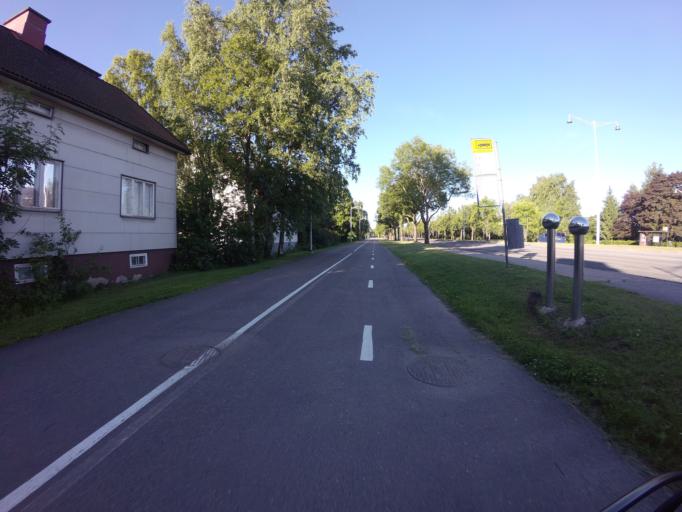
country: FI
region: Varsinais-Suomi
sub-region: Turku
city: Turku
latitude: 60.4687
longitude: 22.2789
